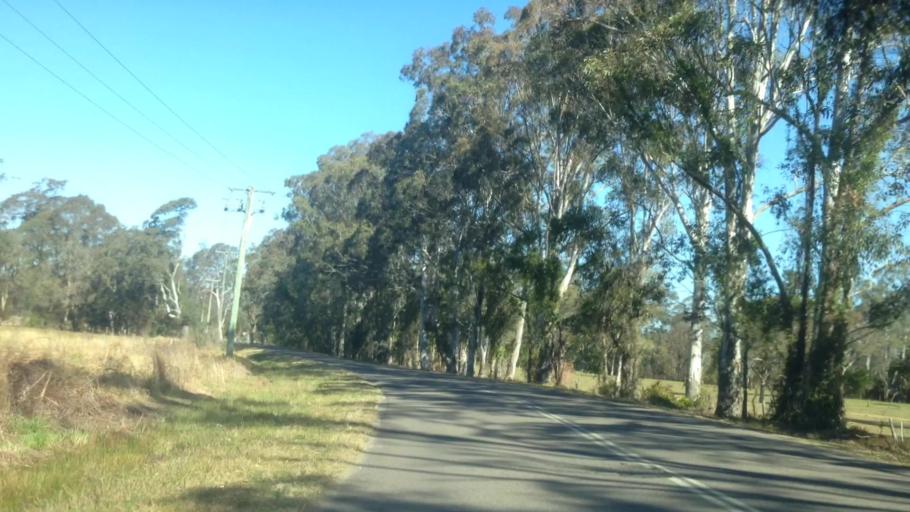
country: AU
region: New South Wales
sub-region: Lake Macquarie Shire
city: Cooranbong
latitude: -33.1169
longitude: 151.4460
